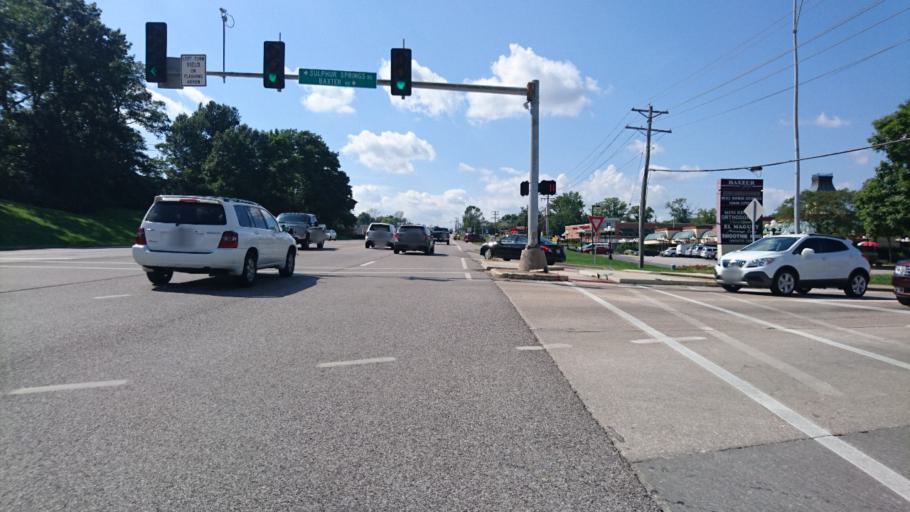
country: US
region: Missouri
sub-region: Saint Louis County
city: Winchester
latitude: 38.5933
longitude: -90.5208
